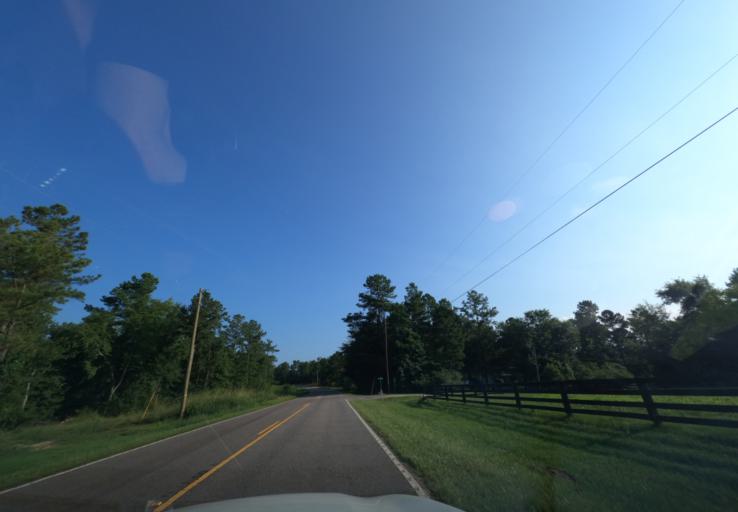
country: US
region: South Carolina
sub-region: Edgefield County
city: Murphys Estates
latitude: 33.6325
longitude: -81.9737
